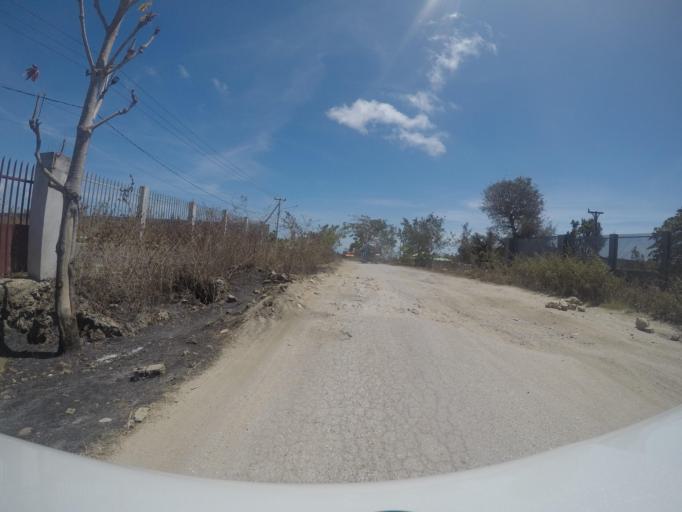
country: TL
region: Baucau
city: Baucau
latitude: -8.4665
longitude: 126.4321
